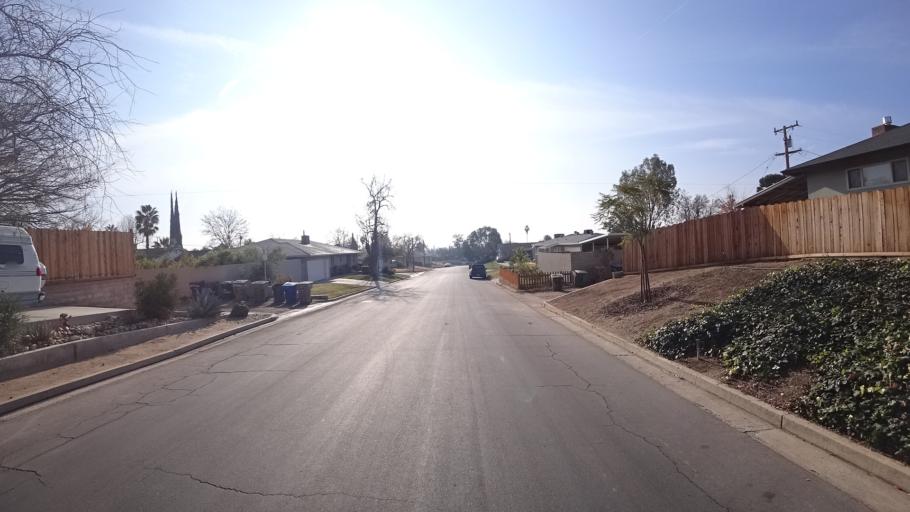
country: US
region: California
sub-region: Kern County
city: Oildale
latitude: 35.4075
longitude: -118.9822
